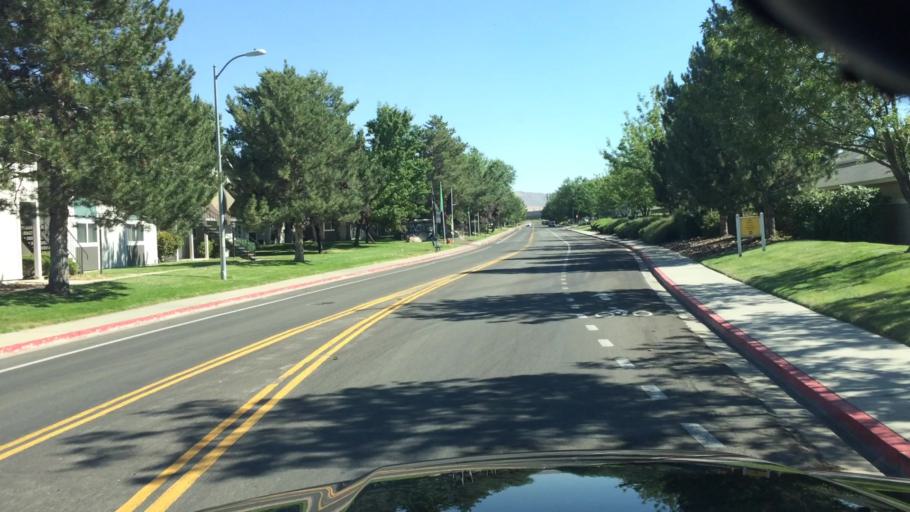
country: US
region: Nevada
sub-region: Washoe County
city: Sparks
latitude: 39.4530
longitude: -119.7712
